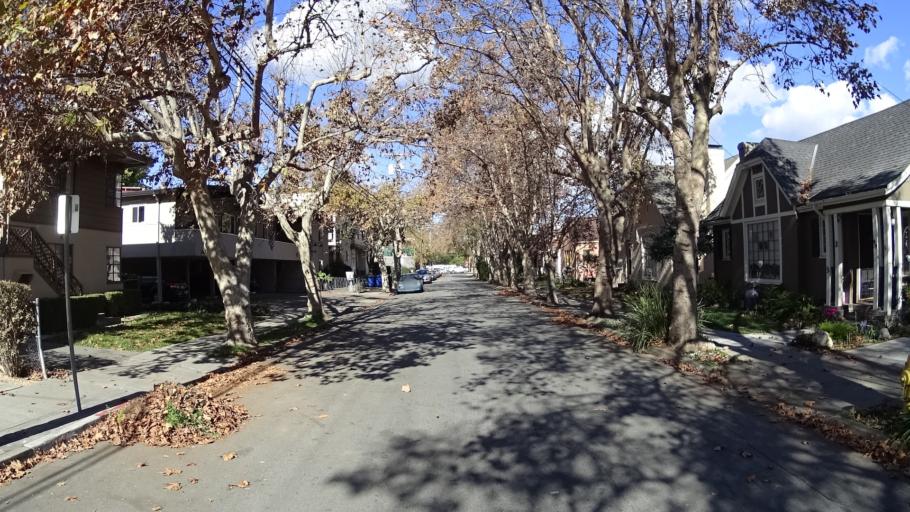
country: US
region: California
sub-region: Santa Clara County
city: Buena Vista
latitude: 37.3302
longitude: -121.9091
